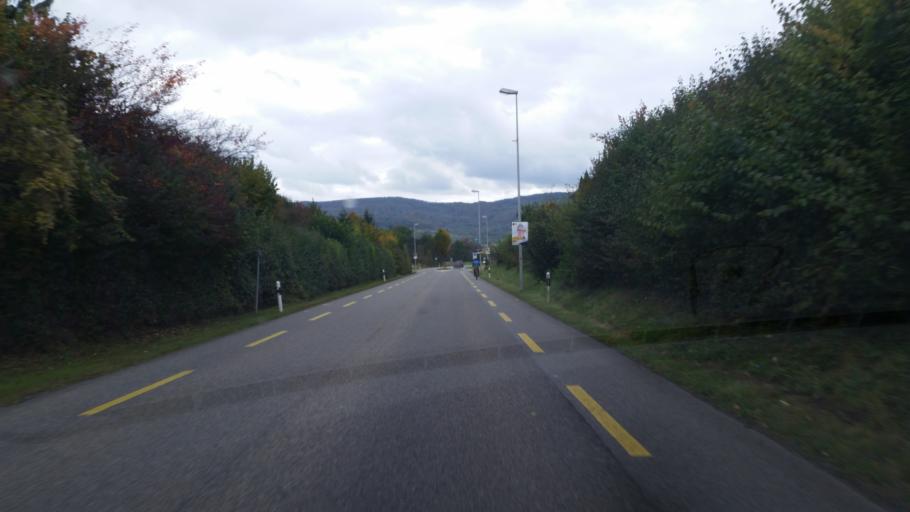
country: CH
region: Aargau
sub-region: Bezirk Baden
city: Unterehrendingen
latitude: 47.5184
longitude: 8.3317
